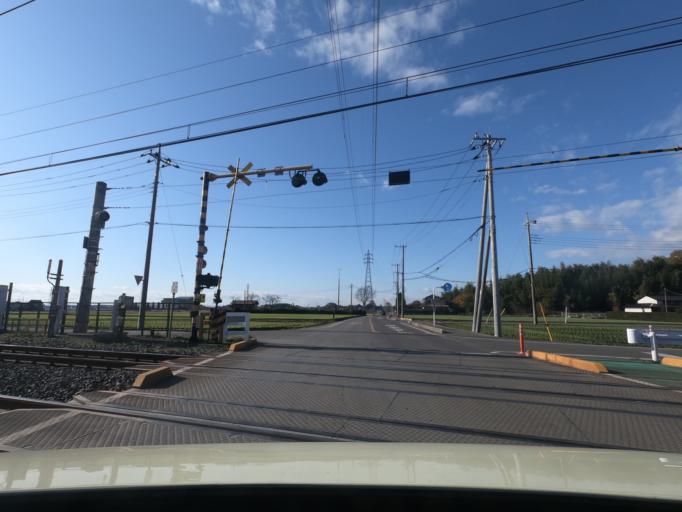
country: JP
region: Ibaraki
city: Koga
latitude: 36.2399
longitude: 139.7448
